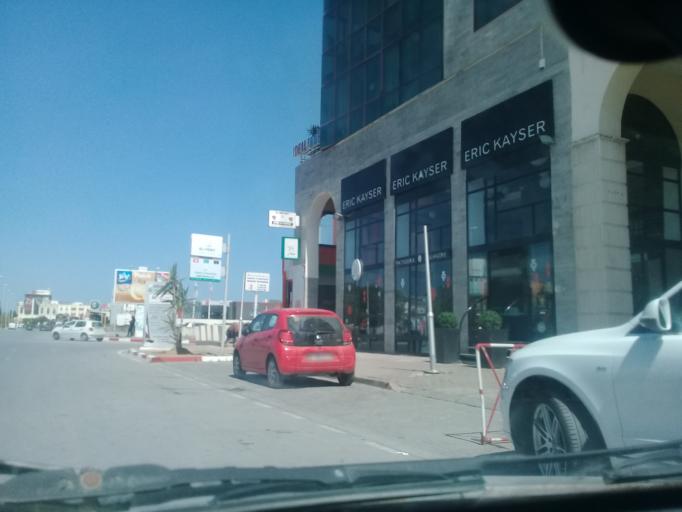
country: TN
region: Ariana
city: Ariana
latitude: 36.8358
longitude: 10.2416
